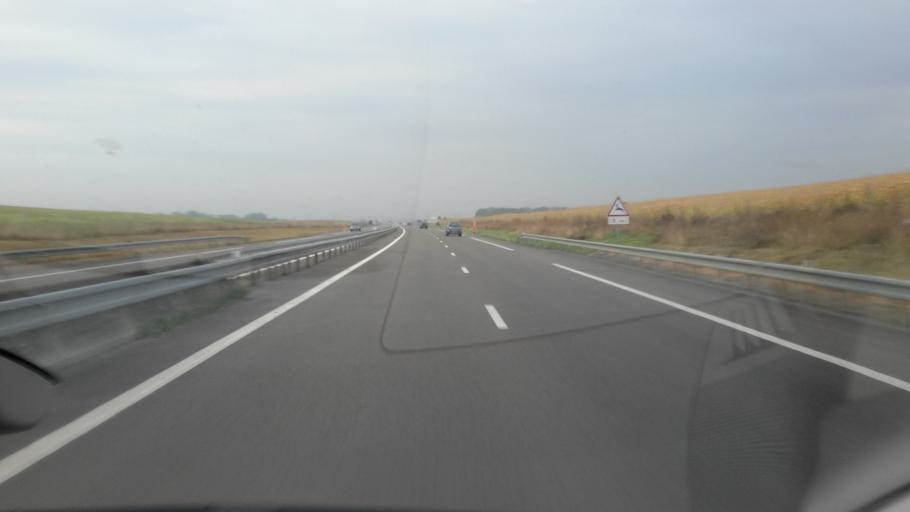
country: FR
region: Champagne-Ardenne
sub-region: Departement des Ardennes
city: Attigny
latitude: 49.5903
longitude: 4.4942
